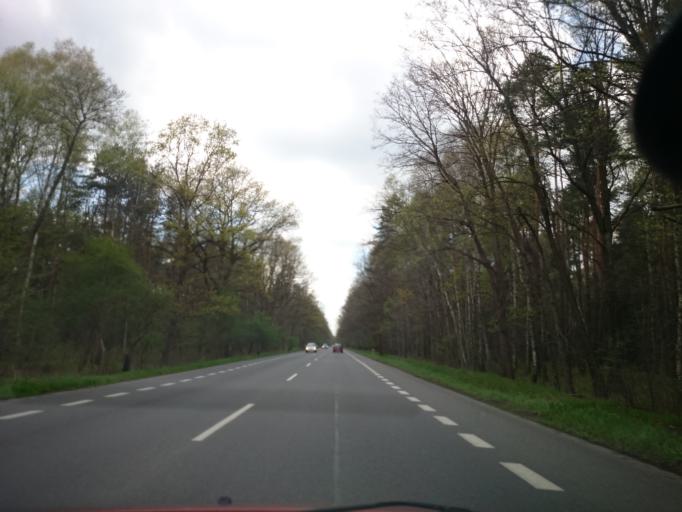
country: PL
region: Opole Voivodeship
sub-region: Powiat opolski
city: Chrzastowice
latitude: 50.6309
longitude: 18.0254
